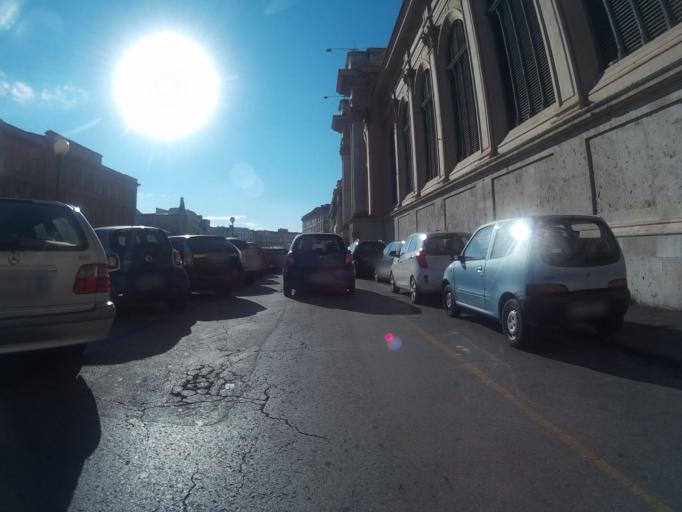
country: IT
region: Tuscany
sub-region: Provincia di Livorno
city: Livorno
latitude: 43.5502
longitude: 10.3133
